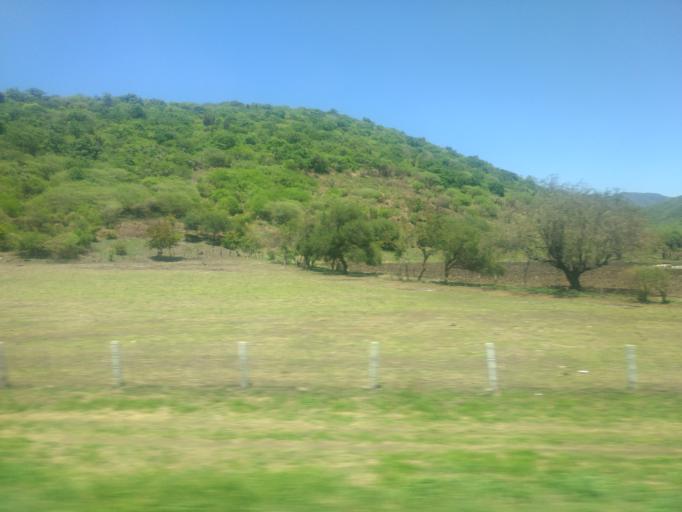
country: MX
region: Jalisco
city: Zacoalco de Torres
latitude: 20.2241
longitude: -103.5328
